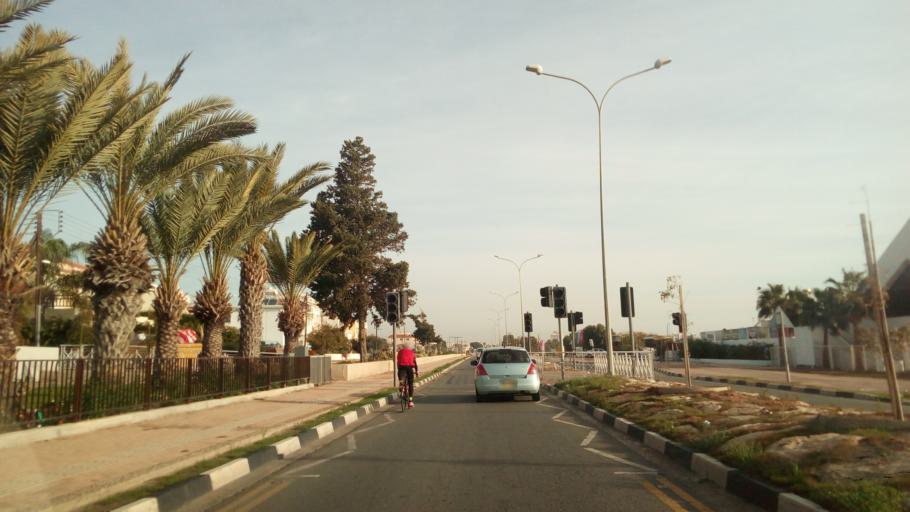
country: CY
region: Larnaka
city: Livadia
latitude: 34.9526
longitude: 33.6502
